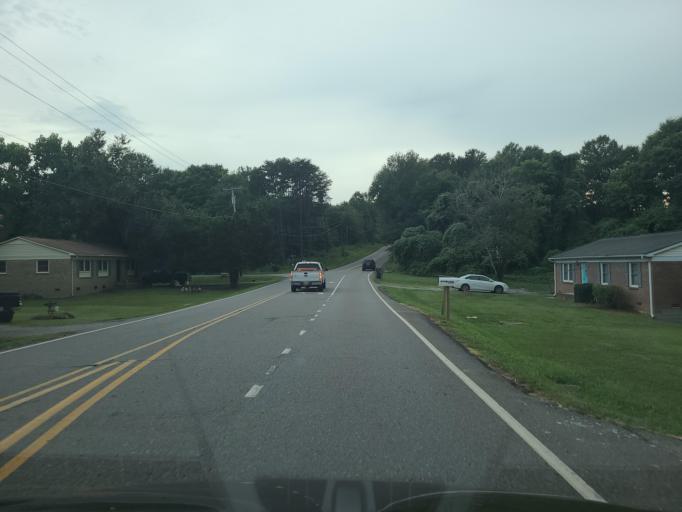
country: US
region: North Carolina
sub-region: Gaston County
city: Dallas
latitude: 35.3017
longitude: -81.1729
